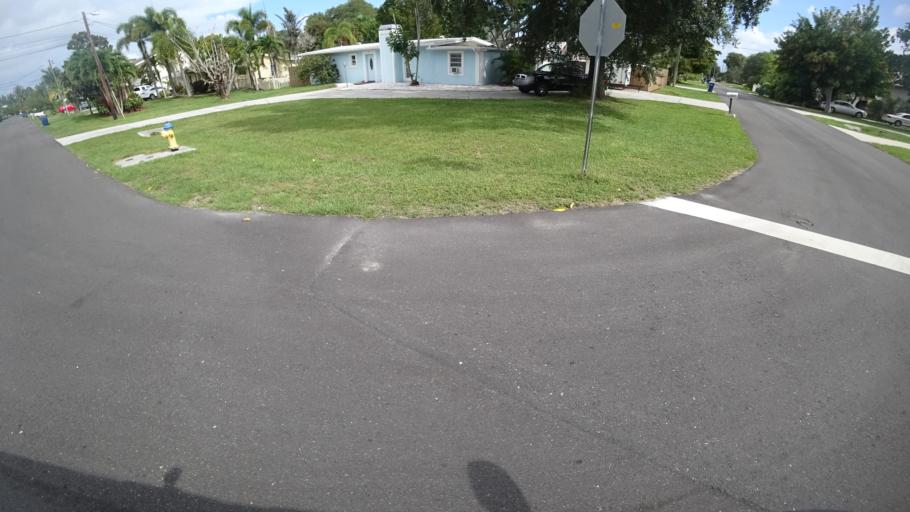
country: US
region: Florida
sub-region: Manatee County
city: Cortez
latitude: 27.4589
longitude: -82.6626
